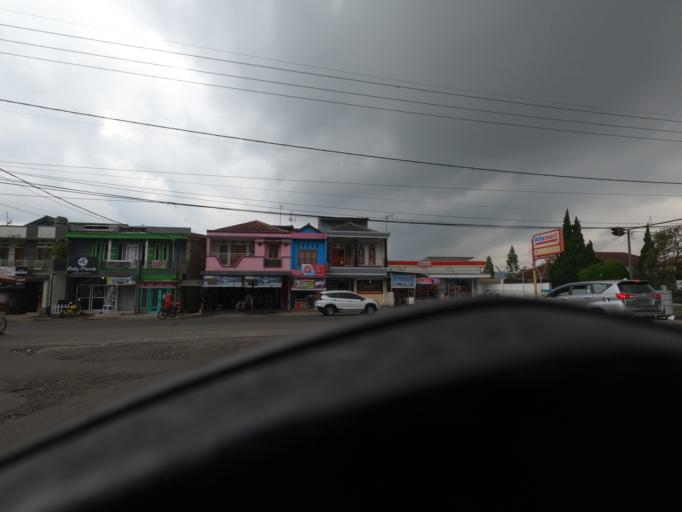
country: ID
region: West Java
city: Lembang
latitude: -6.8119
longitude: 107.6344
